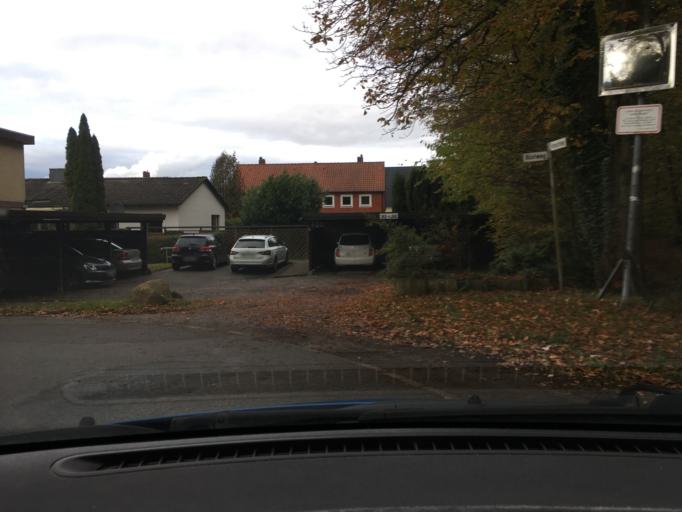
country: DE
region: Lower Saxony
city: Seevetal
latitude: 53.4169
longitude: 9.9913
